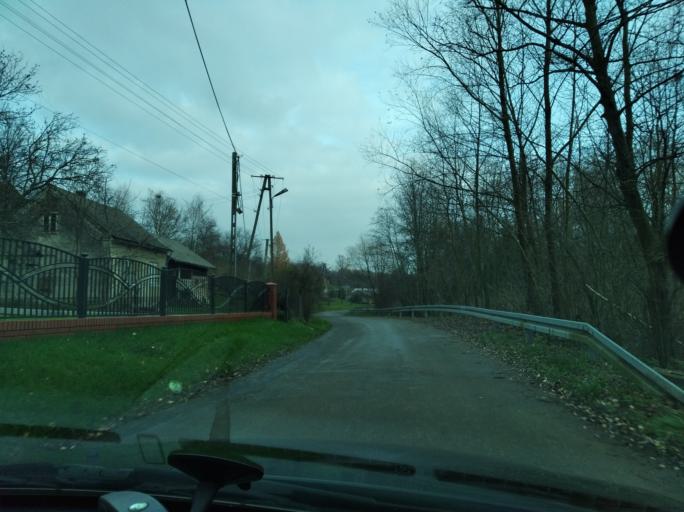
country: PL
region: Subcarpathian Voivodeship
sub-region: Powiat przeworski
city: Sietesz
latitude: 49.9664
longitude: 22.3557
